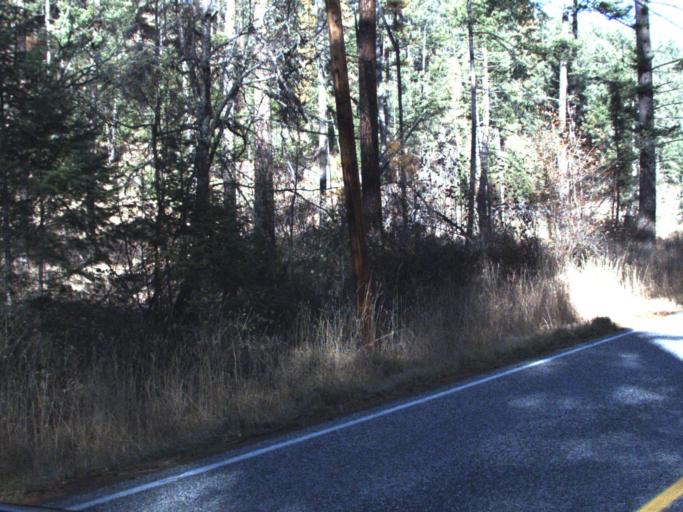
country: CA
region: British Columbia
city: Grand Forks
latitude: 48.9660
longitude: -118.5272
